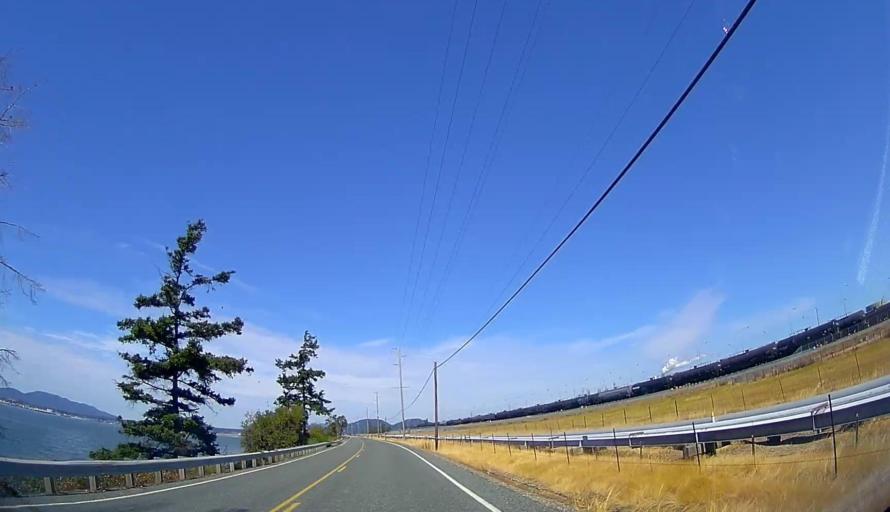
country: US
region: Washington
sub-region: Skagit County
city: Anacortes
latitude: 48.4806
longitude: -122.5733
